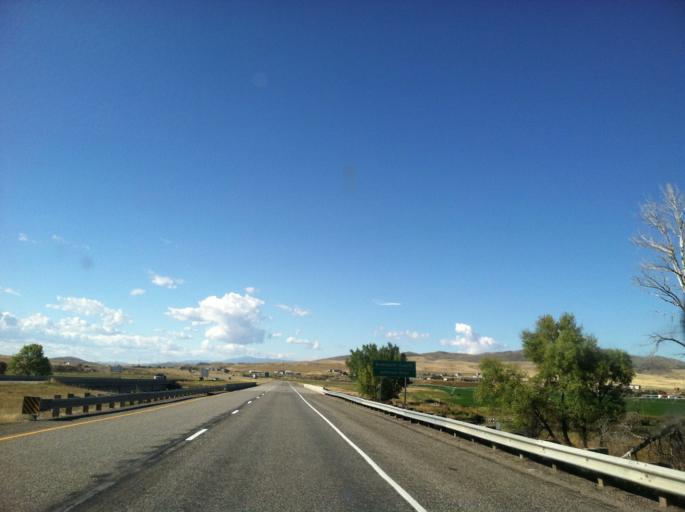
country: US
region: Montana
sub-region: Gallatin County
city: Three Forks
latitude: 45.9099
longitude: -111.5471
